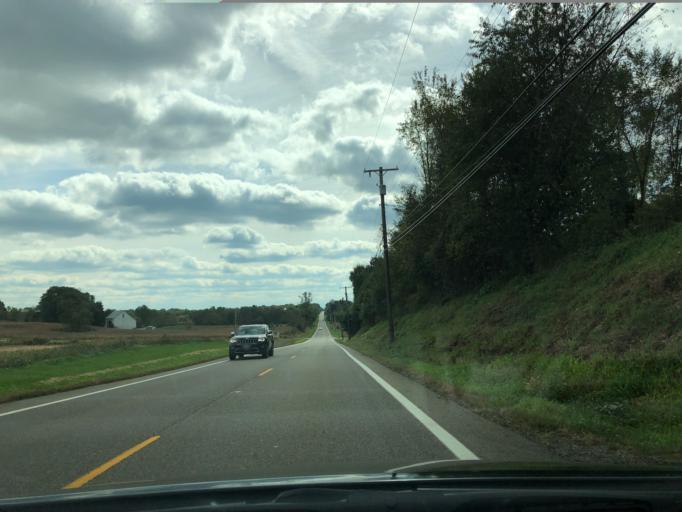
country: US
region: Ohio
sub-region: Stark County
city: Brewster
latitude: 40.7373
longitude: -81.5961
